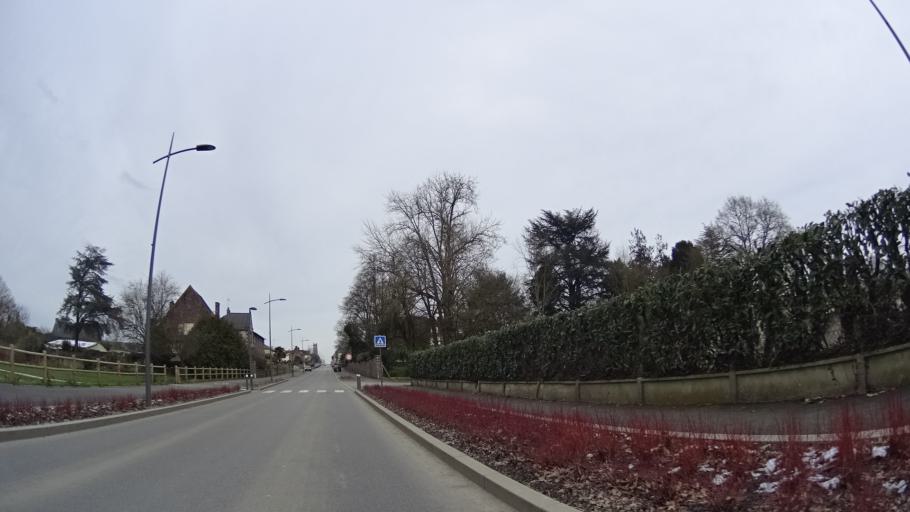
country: FR
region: Brittany
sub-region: Departement d'Ille-et-Vilaine
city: Montauban-de-Bretagne
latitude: 48.1933
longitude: -2.0502
